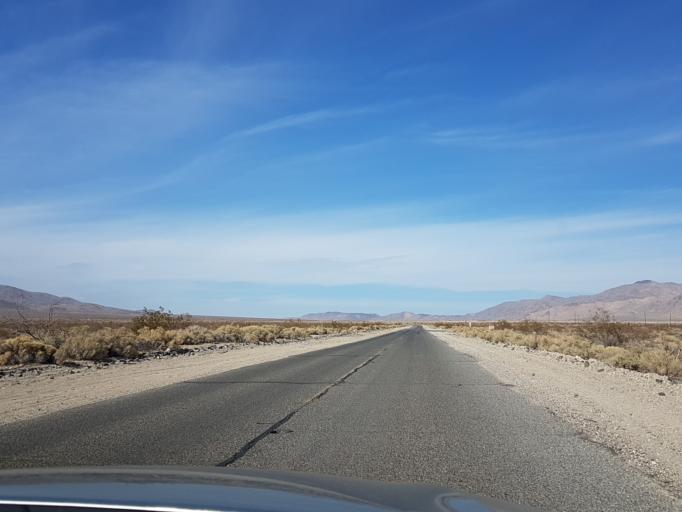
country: US
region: California
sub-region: San Bernardino County
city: Searles Valley
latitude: 35.8272
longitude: -117.3392
